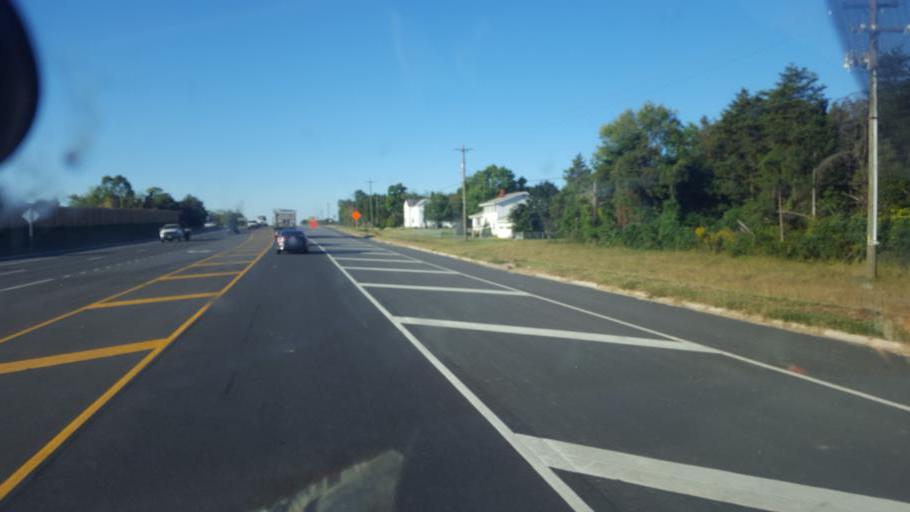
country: US
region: Virginia
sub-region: Prince William County
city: Nokesville
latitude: 38.7218
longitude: -77.5564
